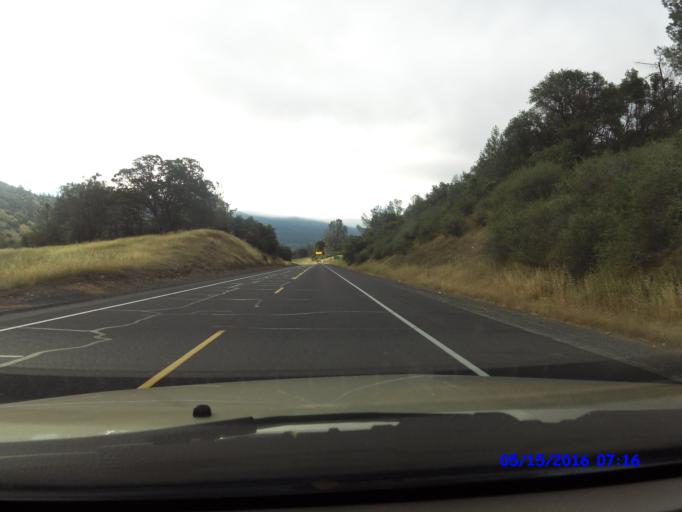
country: US
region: California
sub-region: Tuolumne County
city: Tuolumne City
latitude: 37.8167
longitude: -120.3181
